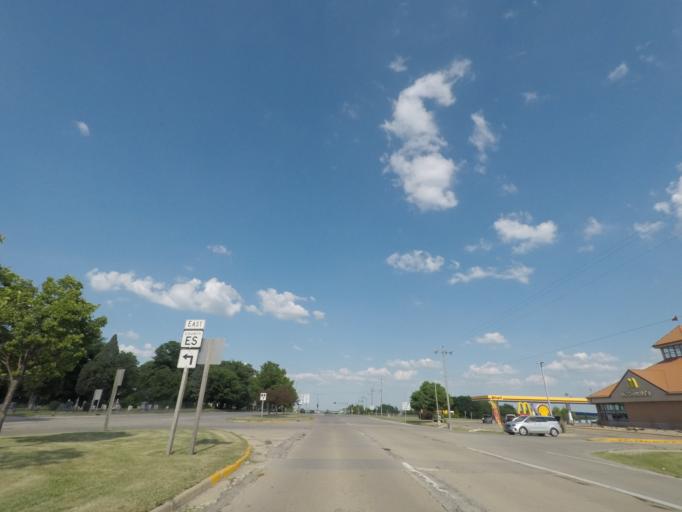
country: US
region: Wisconsin
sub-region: Walworth County
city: East Troy
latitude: 42.7921
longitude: -88.3918
